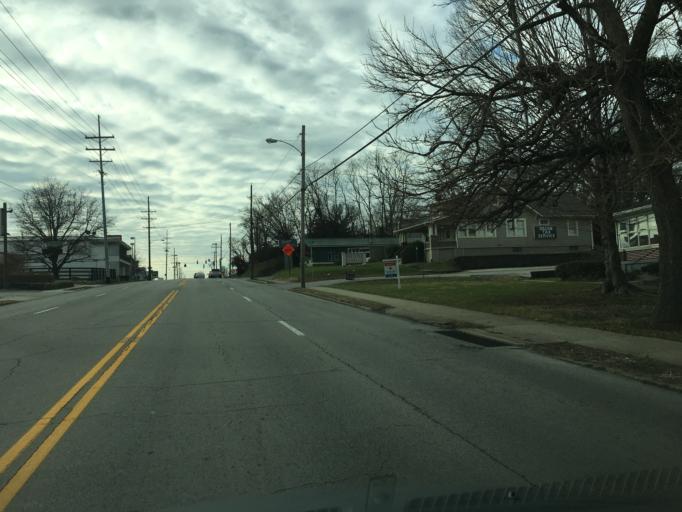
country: US
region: Kentucky
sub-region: Franklin County
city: Frankfort
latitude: 38.2042
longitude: -84.8440
